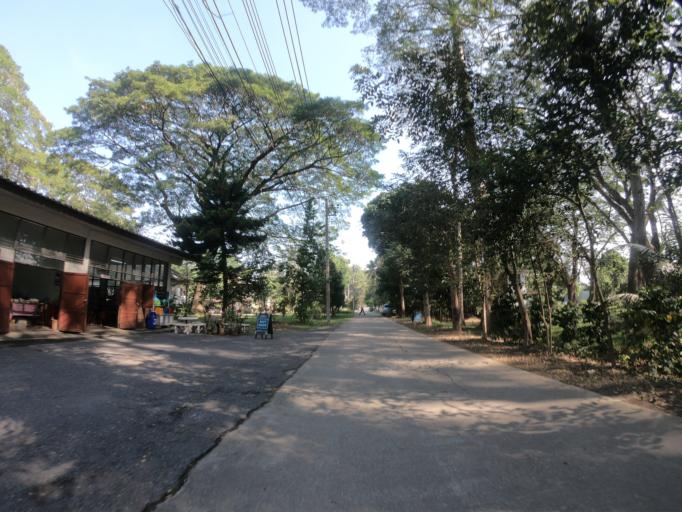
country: TH
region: Chiang Mai
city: Saraphi
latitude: 18.7325
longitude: 98.9877
